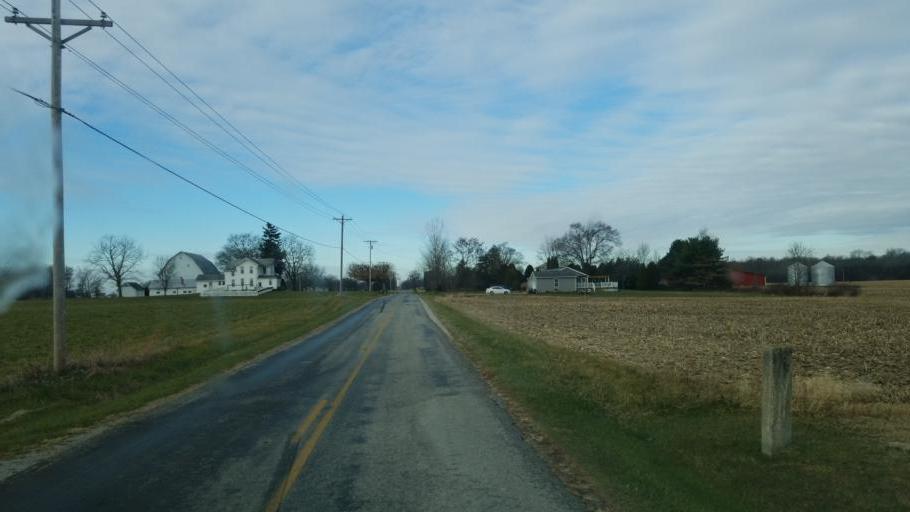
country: US
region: Ohio
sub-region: Morrow County
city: Cardington
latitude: 40.6017
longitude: -82.9861
